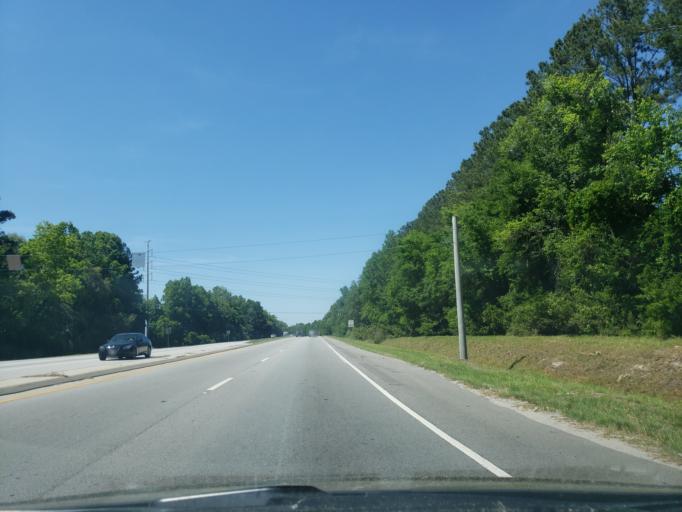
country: US
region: Georgia
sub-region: Chatham County
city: Montgomery
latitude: 31.9590
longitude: -81.0985
